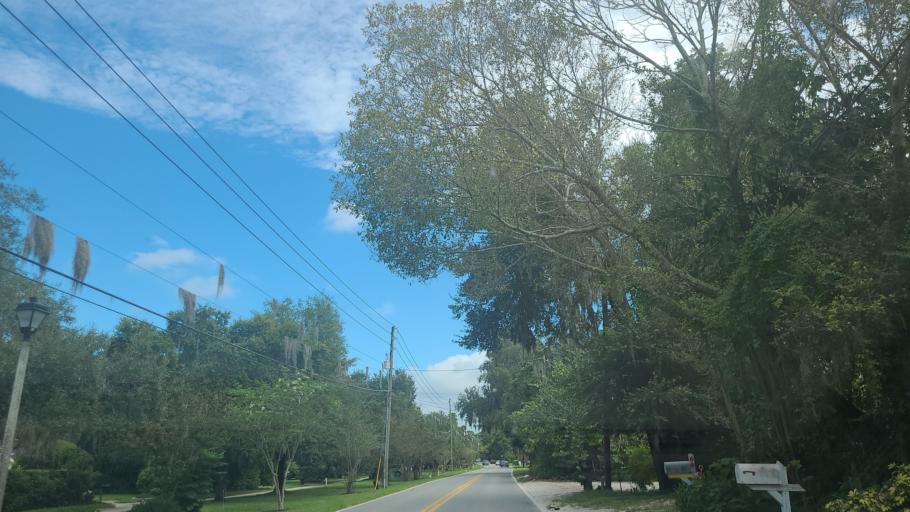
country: US
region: Florida
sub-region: Orange County
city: Lake Butler
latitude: 28.5009
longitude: -81.5369
